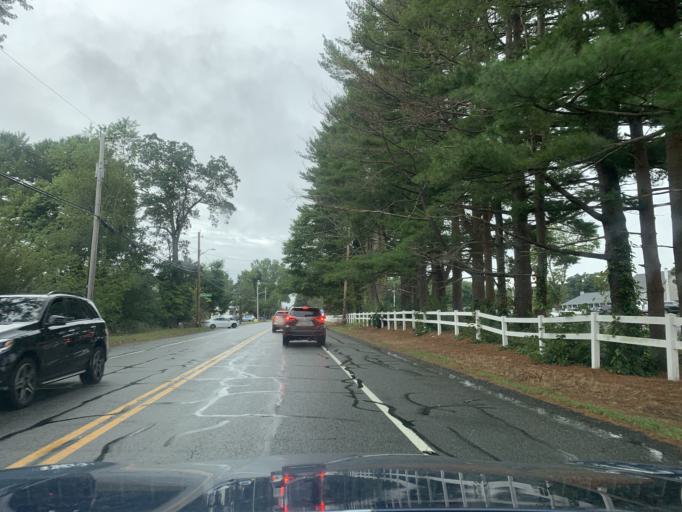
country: US
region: Rhode Island
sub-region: Bristol County
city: Warren
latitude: 41.7627
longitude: -71.2689
